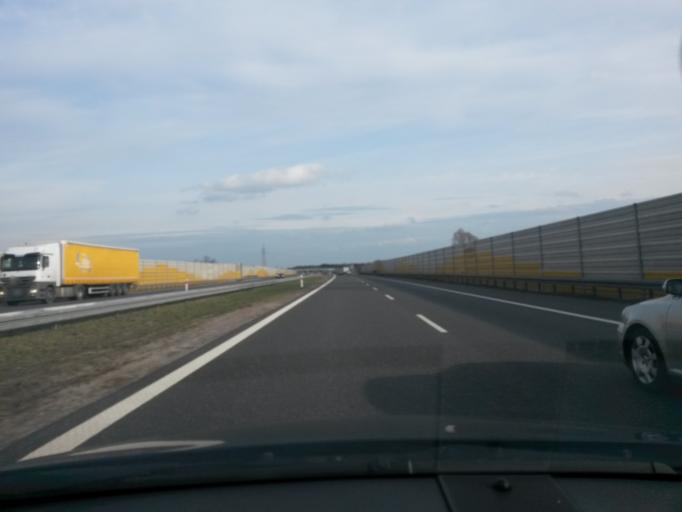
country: PL
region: Greater Poland Voivodeship
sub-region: Powiat kolski
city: Dabie
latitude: 52.0430
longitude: 18.8595
